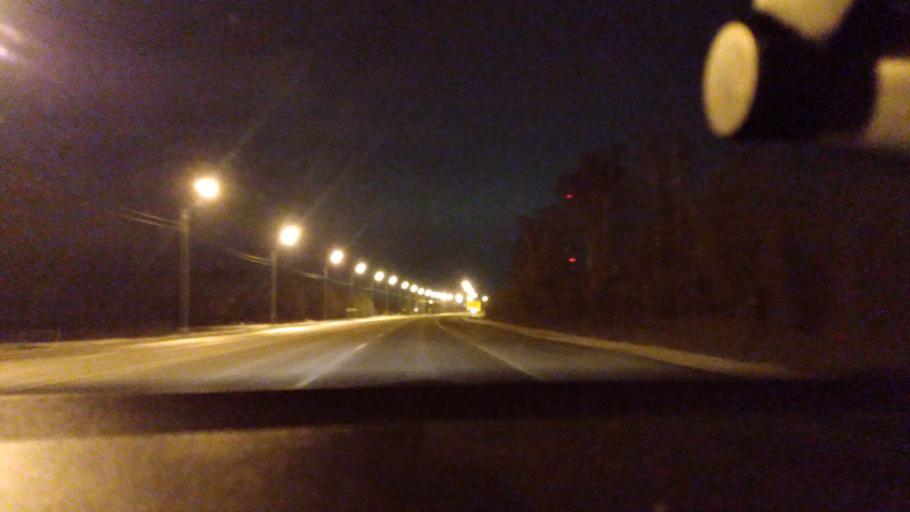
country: RU
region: Moskovskaya
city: Bronnitsy
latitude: 55.3907
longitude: 38.3303
